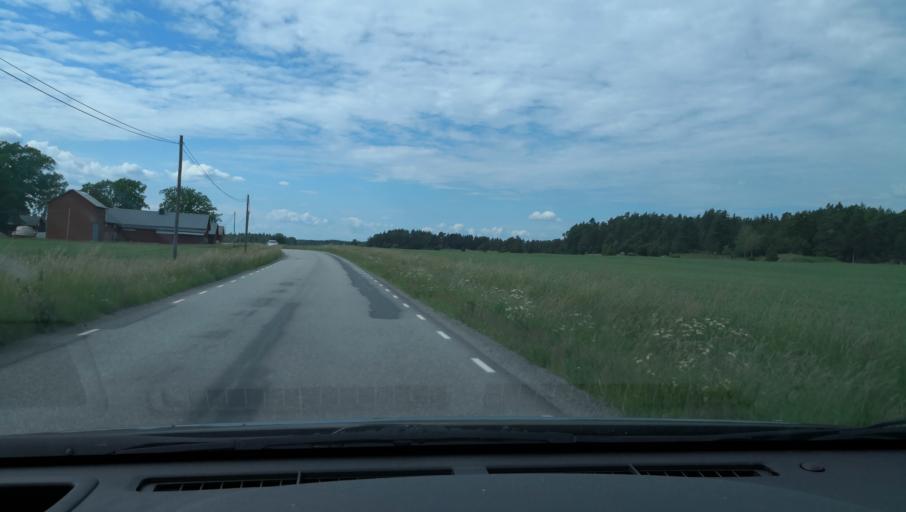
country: SE
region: Uppsala
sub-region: Uppsala Kommun
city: Uppsala
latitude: 59.8117
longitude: 17.5112
